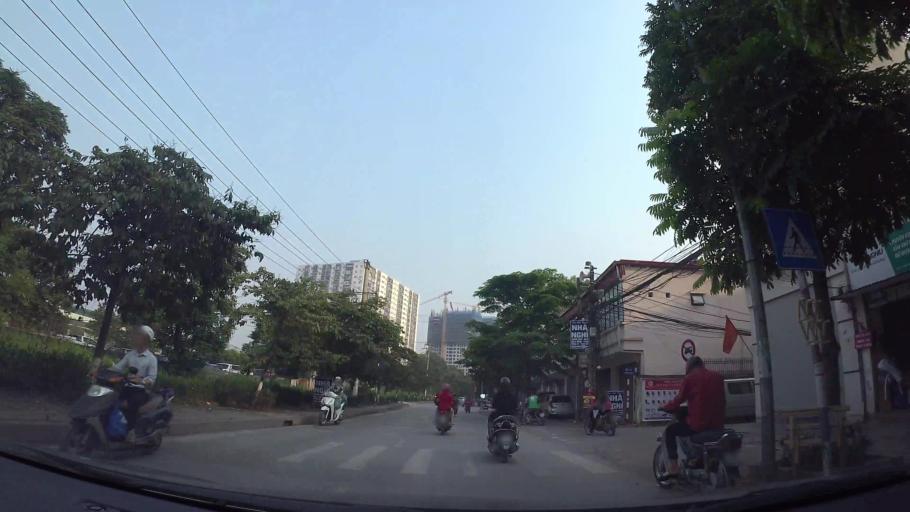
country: VN
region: Ha Noi
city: Thanh Xuan
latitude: 20.9769
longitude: 105.8244
